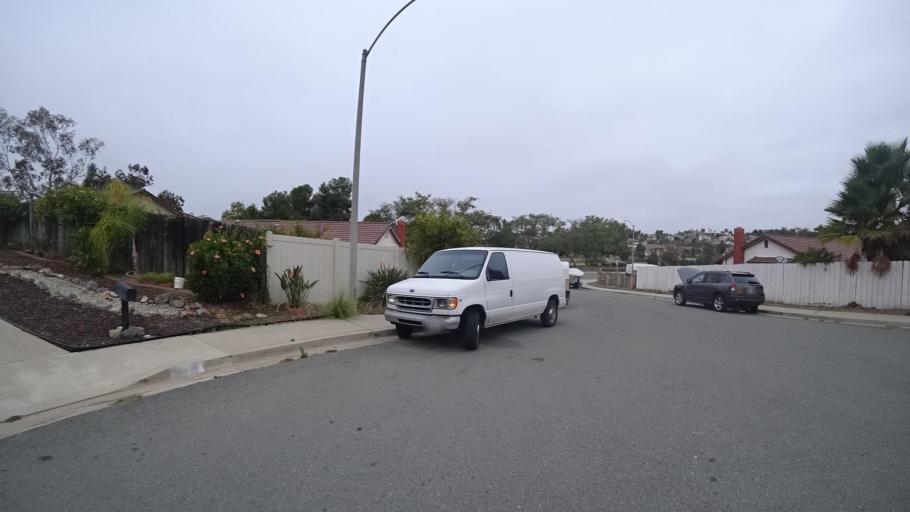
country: US
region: California
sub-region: San Diego County
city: Rancho San Diego
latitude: 32.7562
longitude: -116.9116
